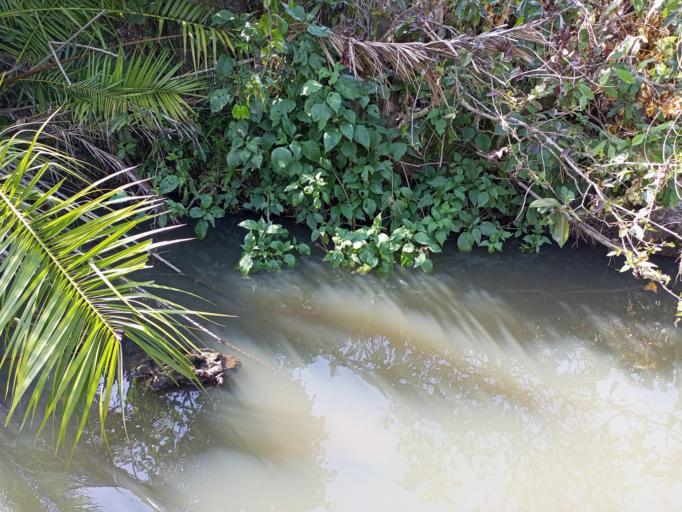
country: CD
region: Eastern Province
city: Bunia
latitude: 1.5355
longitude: 30.2959
